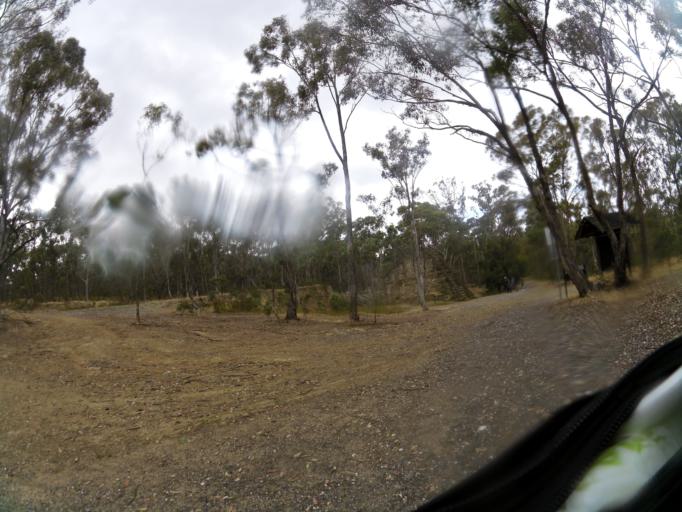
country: AU
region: Victoria
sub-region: Mount Alexander
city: Castlemaine
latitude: -37.0718
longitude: 144.2591
